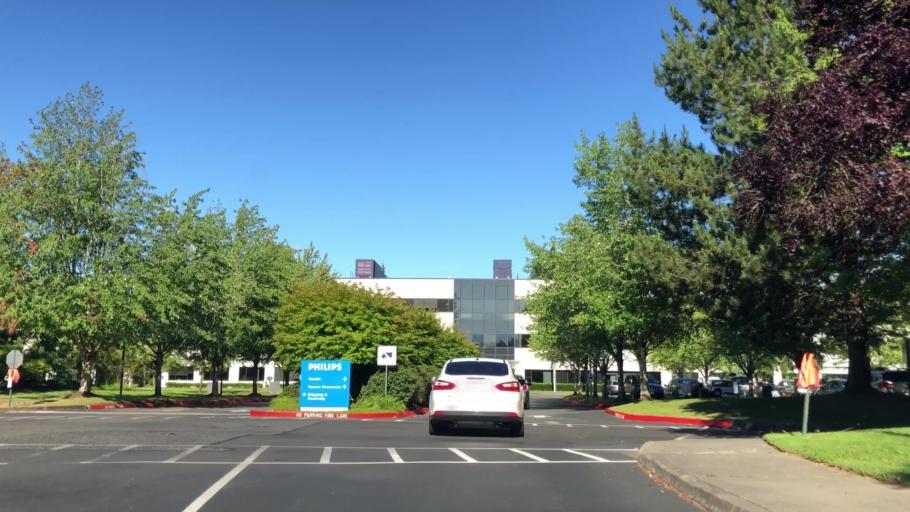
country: US
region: Washington
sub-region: King County
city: Bothell
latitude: 47.7987
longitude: -122.2138
